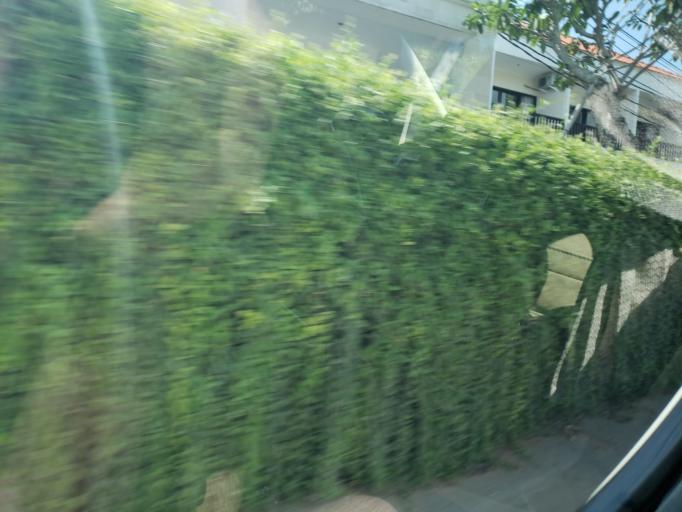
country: ID
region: Bali
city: Kangin
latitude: -8.8292
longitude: 115.1496
